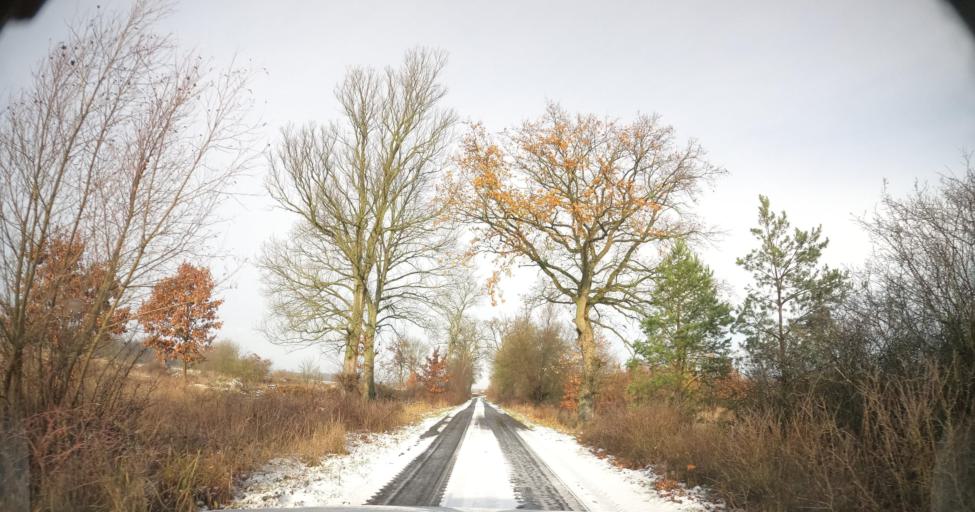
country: PL
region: West Pomeranian Voivodeship
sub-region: Powiat gryfinski
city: Mieszkowice
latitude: 52.7619
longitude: 14.4864
